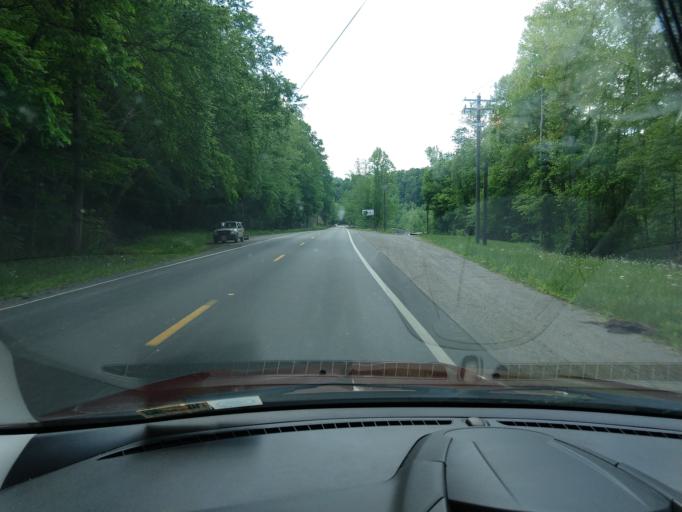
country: US
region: West Virginia
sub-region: Gilmer County
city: Glenville
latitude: 38.9154
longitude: -80.7641
